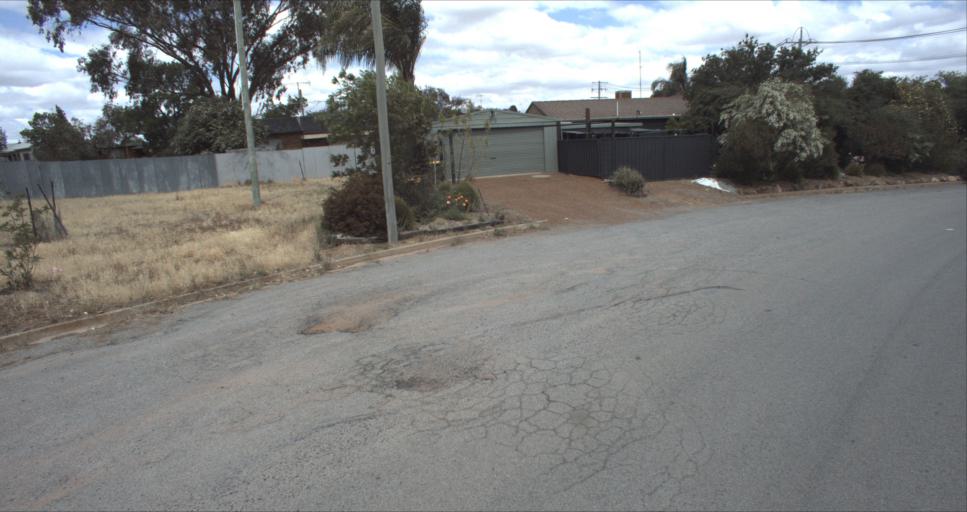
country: AU
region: New South Wales
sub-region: Leeton
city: Leeton
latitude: -34.5606
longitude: 146.3935
